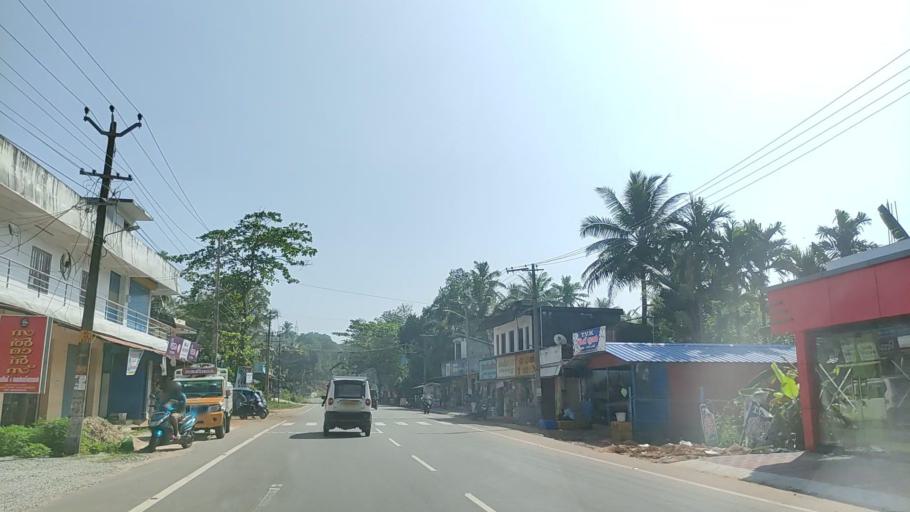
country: IN
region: Kerala
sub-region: Kollam
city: Punalur
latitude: 8.9350
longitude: 76.9586
